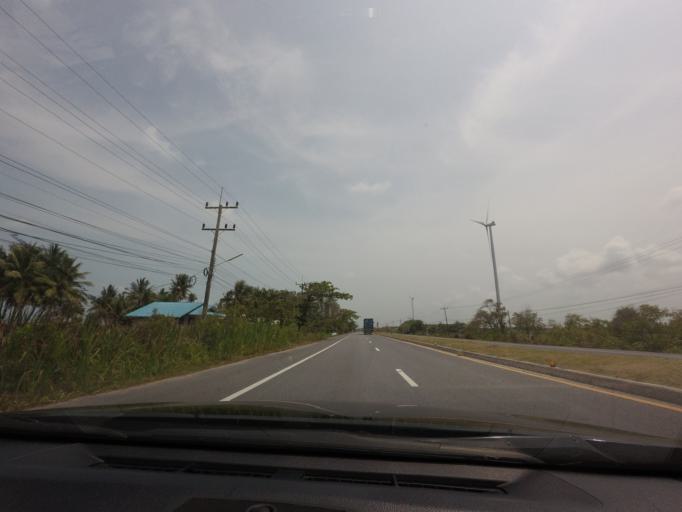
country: TH
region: Nakhon Si Thammarat
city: Hua Sai
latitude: 7.9592
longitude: 100.3301
